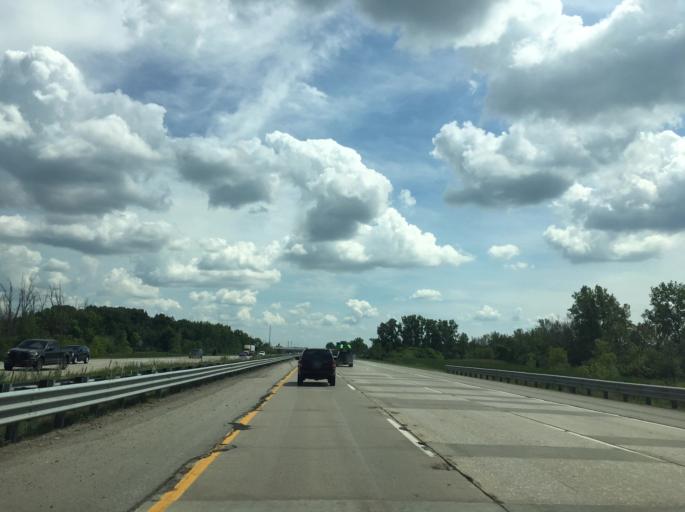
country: US
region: Michigan
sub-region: Saginaw County
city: Zilwaukee
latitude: 43.5056
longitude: -83.9331
